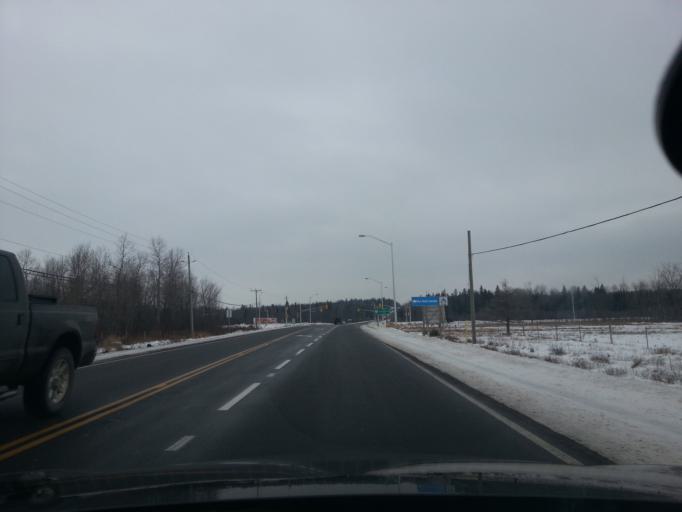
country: CA
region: Ontario
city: Carleton Place
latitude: 45.2693
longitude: -76.1250
